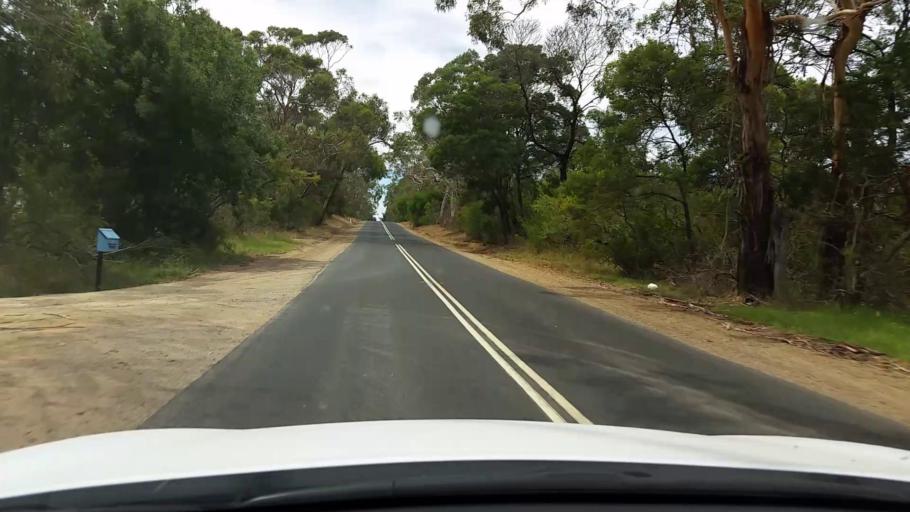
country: AU
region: Victoria
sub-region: Mornington Peninsula
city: Mount Martha
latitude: -38.2942
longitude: 145.0492
